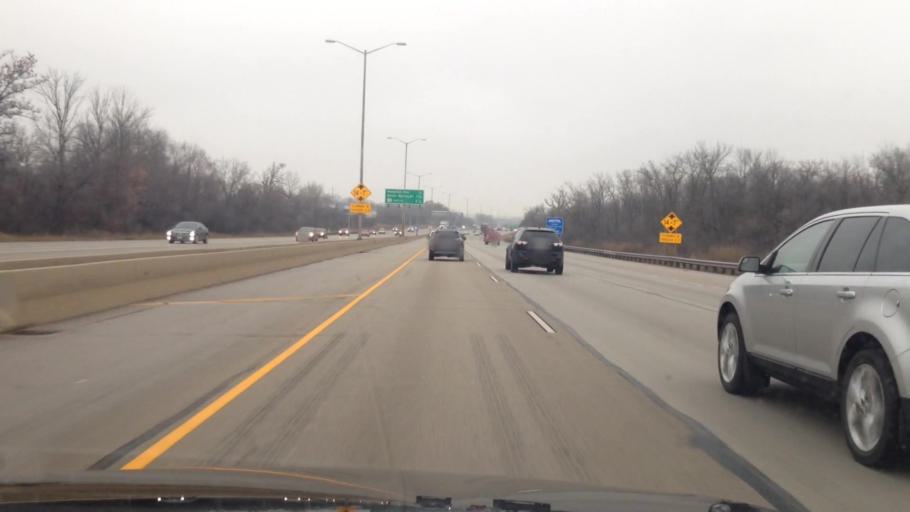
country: US
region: Wisconsin
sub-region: Waukesha County
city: Butler
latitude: 43.0947
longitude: -88.0581
